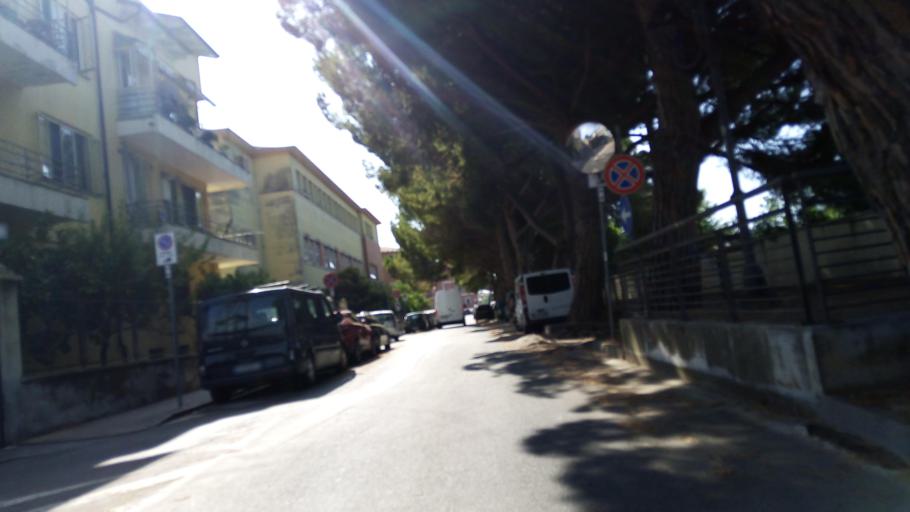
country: IT
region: Liguria
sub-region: Provincia di Savona
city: Albenga
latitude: 44.0501
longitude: 8.2091
